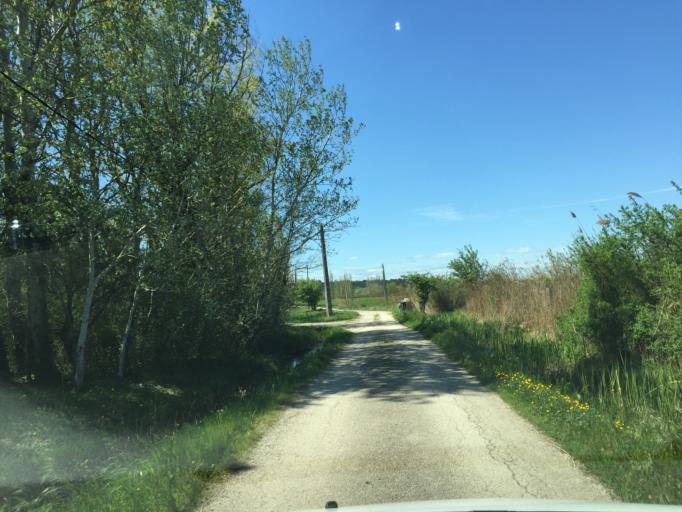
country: FR
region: Provence-Alpes-Cote d'Azur
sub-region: Departement du Vaucluse
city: Courthezon
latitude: 44.0910
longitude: 4.8693
